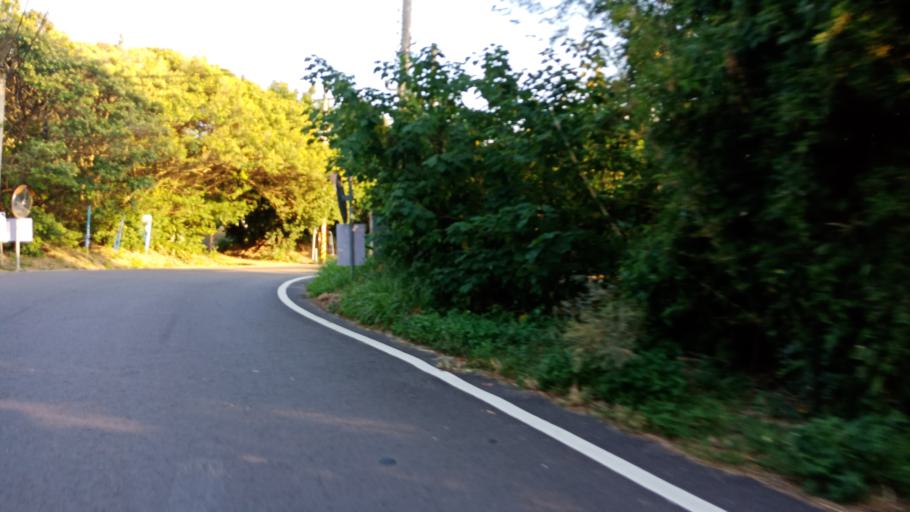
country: TW
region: Taiwan
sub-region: Hsinchu
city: Hsinchu
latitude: 24.7628
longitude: 121.0034
